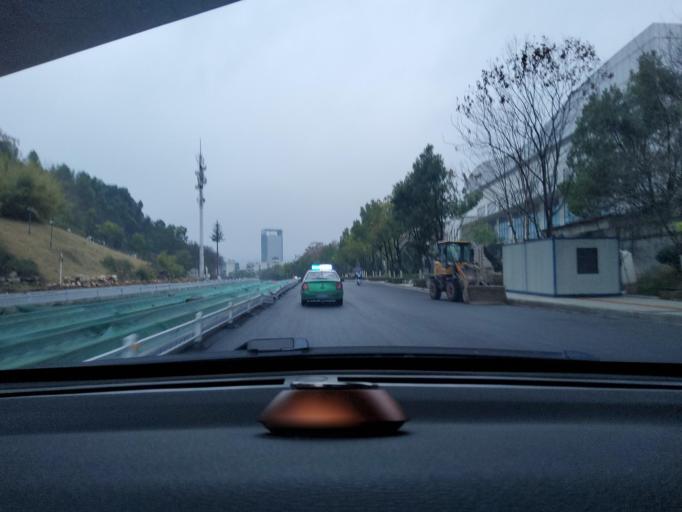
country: CN
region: Hubei
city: Tuanchengshan
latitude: 30.1939
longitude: 115.0231
